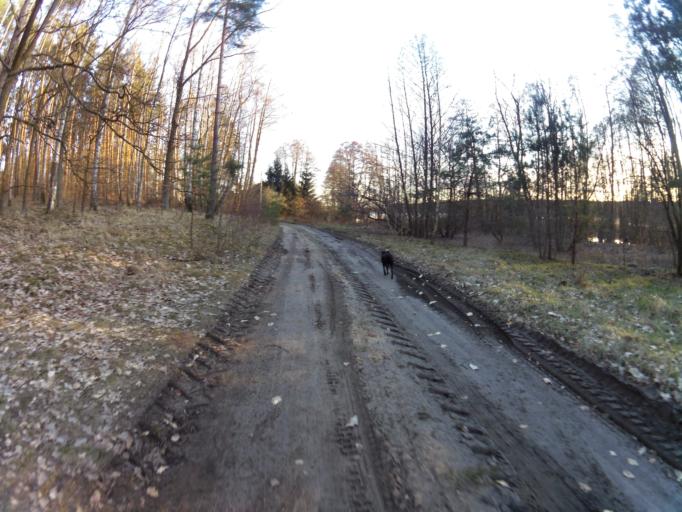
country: PL
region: West Pomeranian Voivodeship
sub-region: Powiat mysliborski
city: Debno
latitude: 52.8266
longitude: 14.7793
